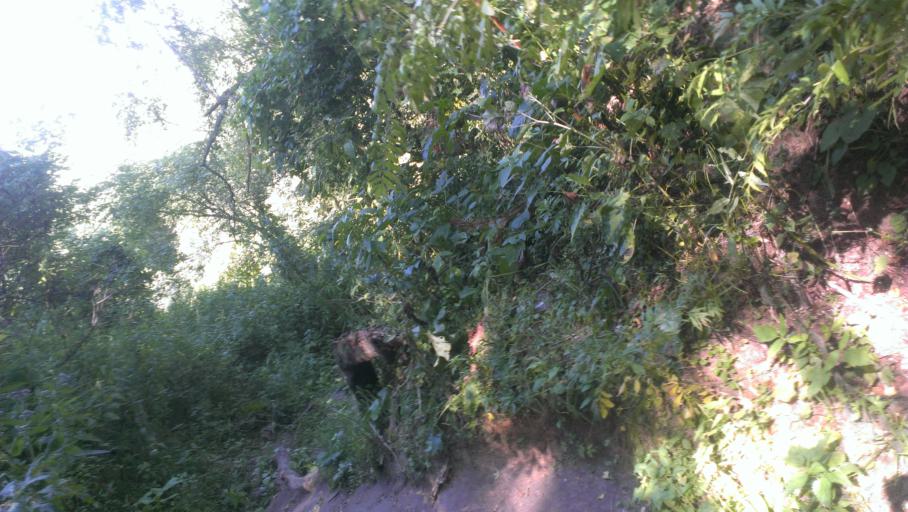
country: RU
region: Altai Krai
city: Nauchnyy Gorodok
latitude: 53.4253
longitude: 83.5049
